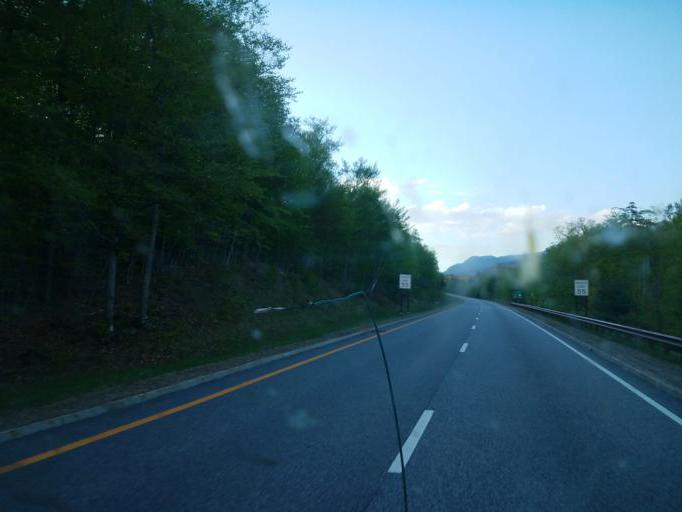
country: US
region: New Hampshire
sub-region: Grafton County
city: Woodstock
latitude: 44.0909
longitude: -71.6850
